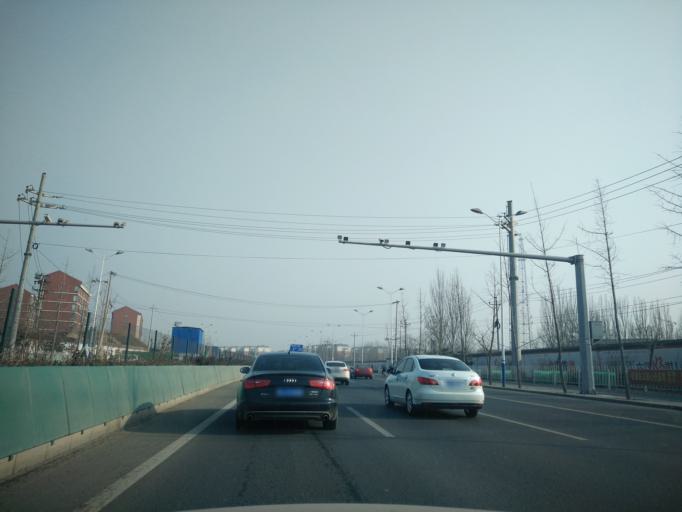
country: CN
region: Beijing
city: Xingfeng
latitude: 39.7401
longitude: 116.3582
